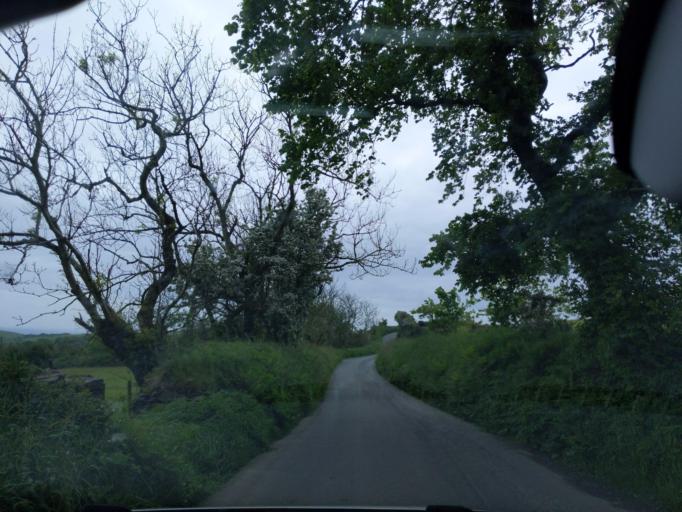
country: IM
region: Douglas
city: Douglas
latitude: 54.1542
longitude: -4.5601
